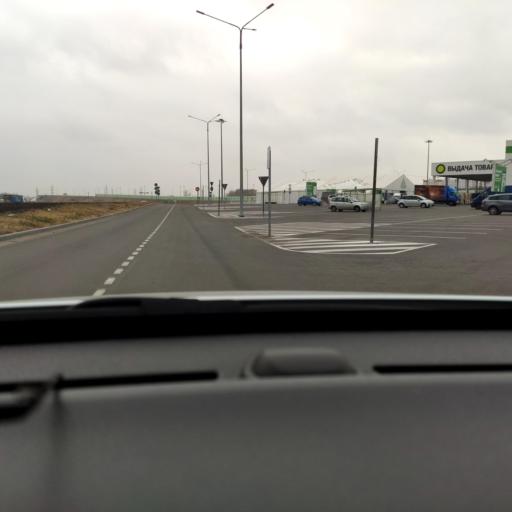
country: RU
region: Voronezj
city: Novaya Usman'
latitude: 51.6506
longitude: 39.3116
